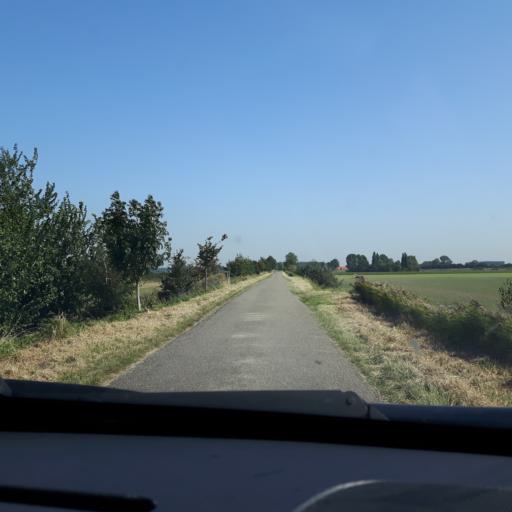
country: NL
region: Zeeland
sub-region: Gemeente Goes
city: Goes
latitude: 51.5024
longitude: 3.7934
